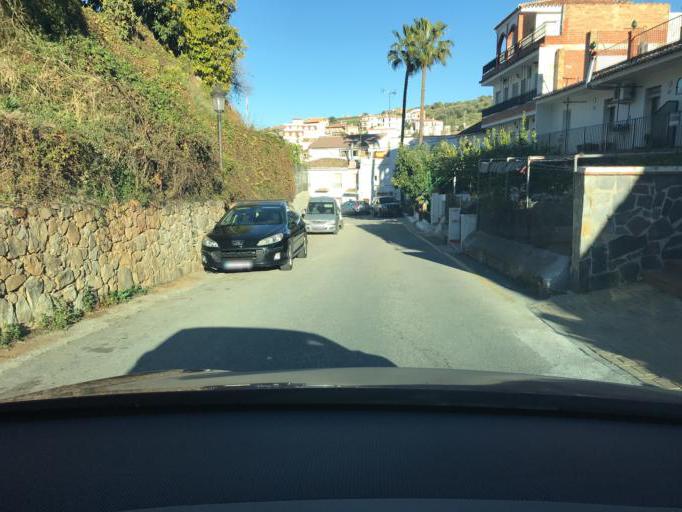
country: ES
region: Andalusia
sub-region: Provincia de Malaga
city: Tolox
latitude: 36.6840
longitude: -4.9056
